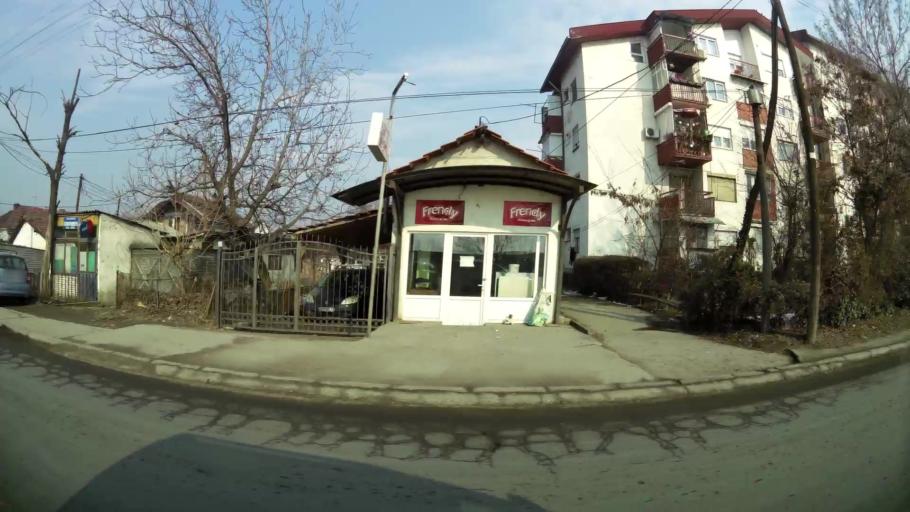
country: MK
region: Kisela Voda
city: Kisela Voda
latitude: 41.9938
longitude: 21.5055
